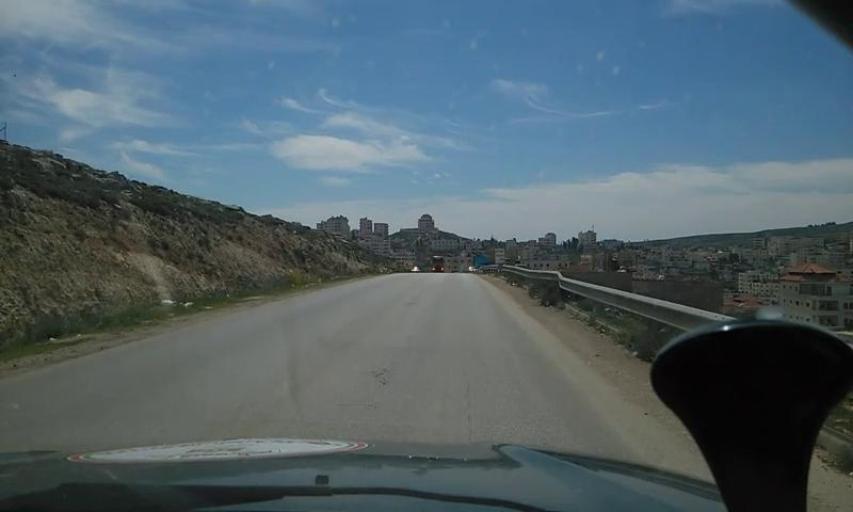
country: PS
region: West Bank
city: Al Judayrah
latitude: 31.8562
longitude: 35.2017
